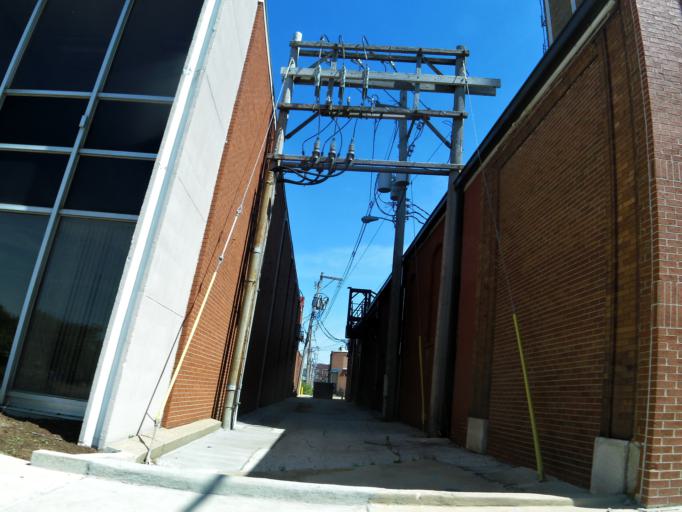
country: US
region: Illinois
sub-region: Vermilion County
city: Danville
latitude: 40.1245
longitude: -87.6306
